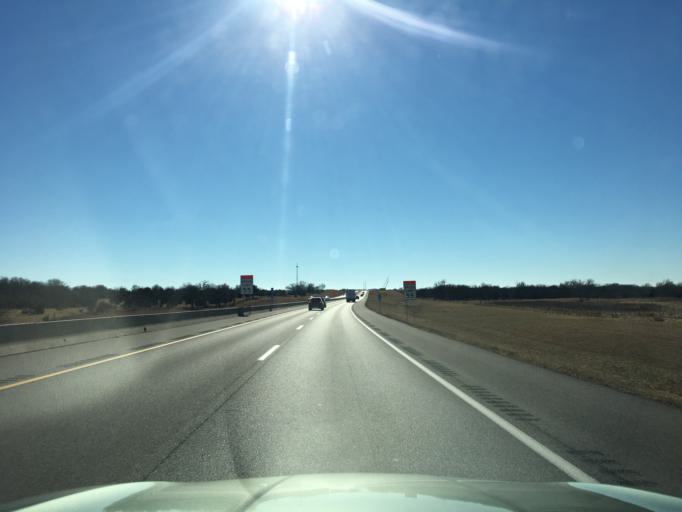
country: US
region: Kansas
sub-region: Sumner County
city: Wellington
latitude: 37.2600
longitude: -97.3391
